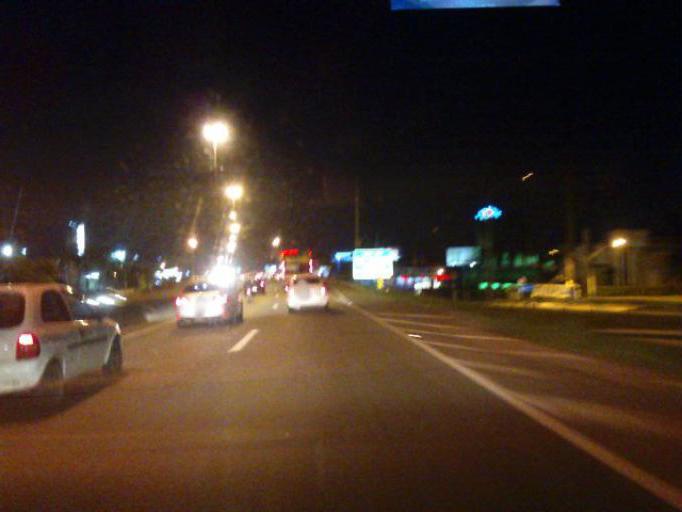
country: BR
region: Santa Catarina
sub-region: Balneario Camboriu
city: Balneario Camboriu
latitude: -26.9963
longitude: -48.6562
